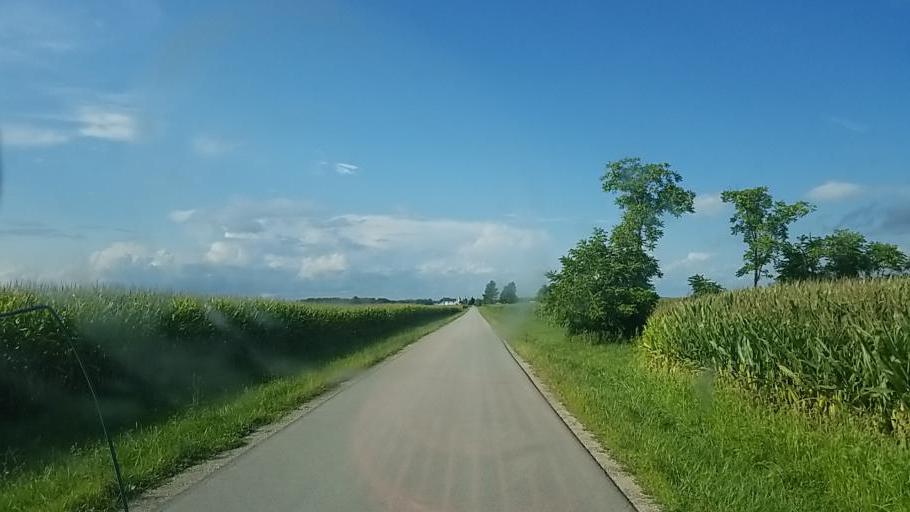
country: US
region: Ohio
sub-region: Wyandot County
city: Upper Sandusky
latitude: 40.7662
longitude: -83.3526
